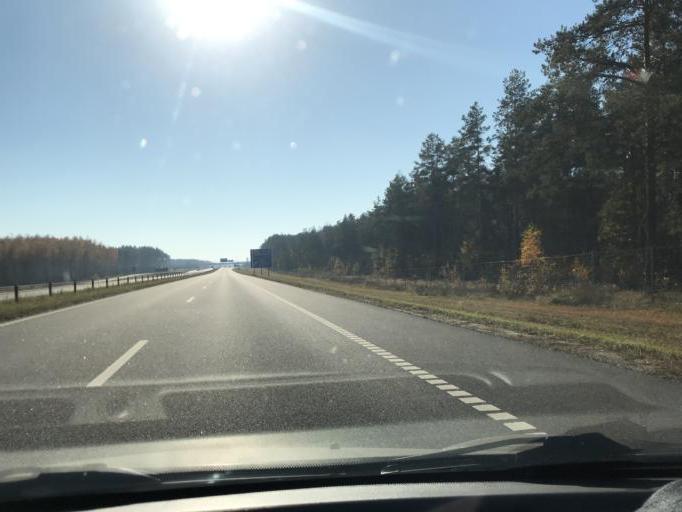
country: BY
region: Mogilev
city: Babruysk
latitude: 53.1516
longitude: 29.3614
